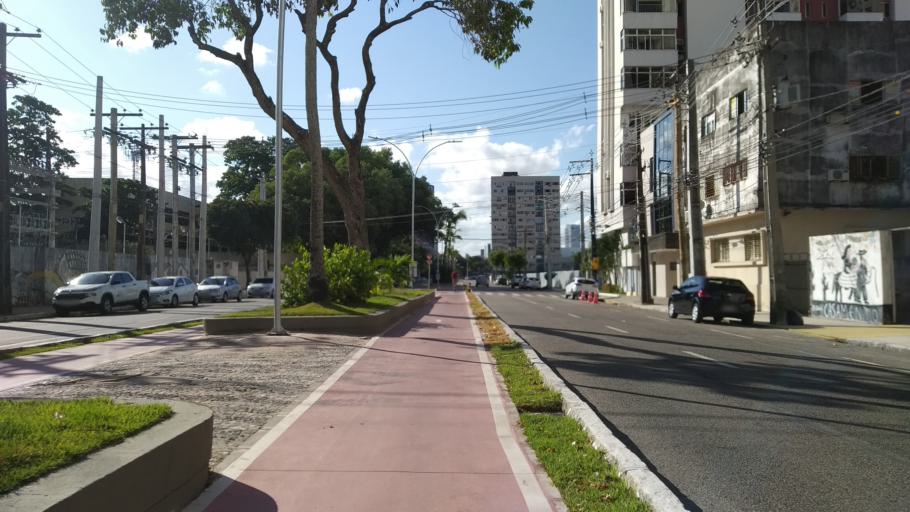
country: BR
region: Pernambuco
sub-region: Recife
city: Recife
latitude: -8.0559
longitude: -34.8785
